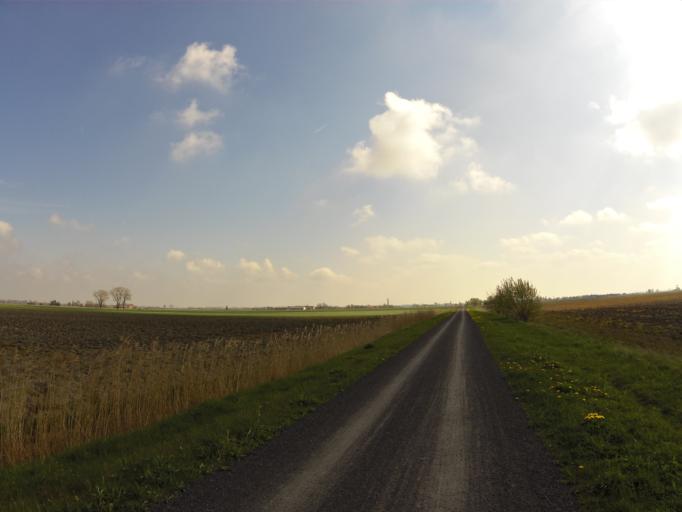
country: BE
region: Flanders
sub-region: Provincie West-Vlaanderen
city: Diksmuide
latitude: 51.0622
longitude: 2.8110
